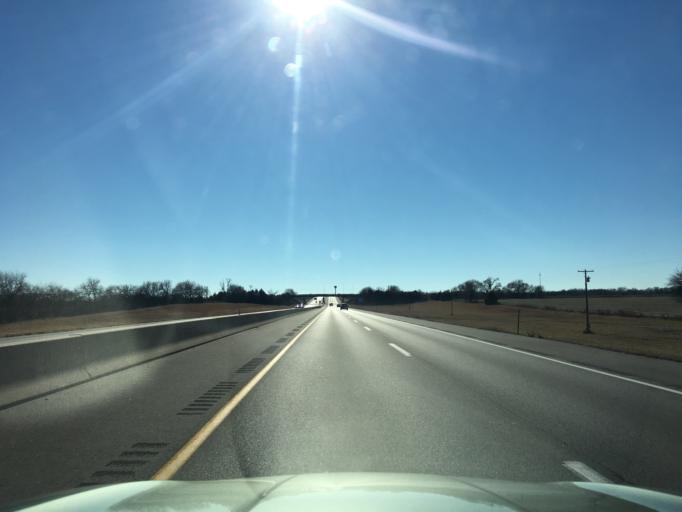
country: US
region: Kansas
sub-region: Sumner County
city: Belle Plaine
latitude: 37.3817
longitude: -97.3242
